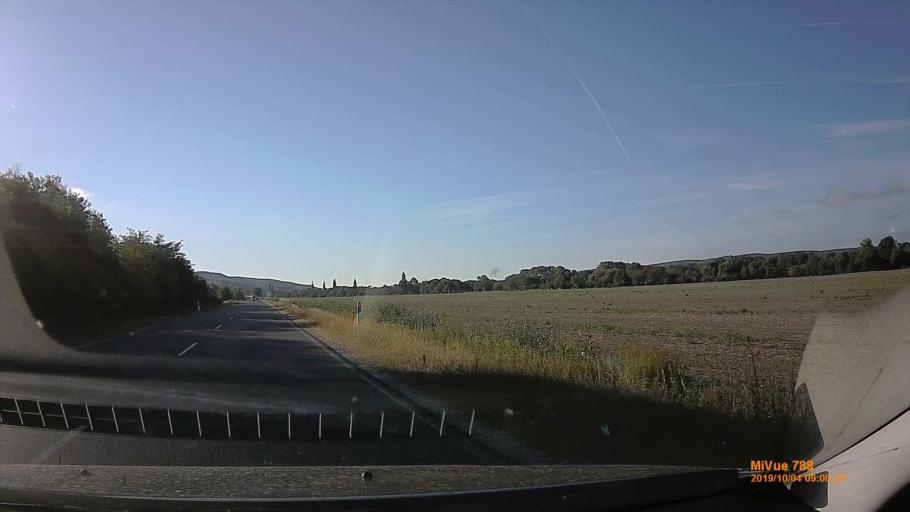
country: HU
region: Somogy
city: Balatonlelle
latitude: 46.7470
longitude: 17.7706
